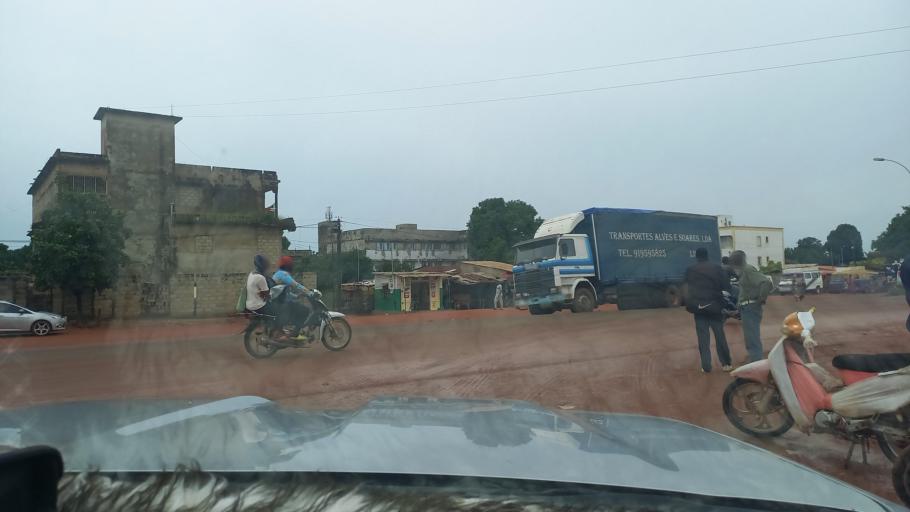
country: SN
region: Ziguinchor
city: Ziguinchor
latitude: 12.5629
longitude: -16.2665
